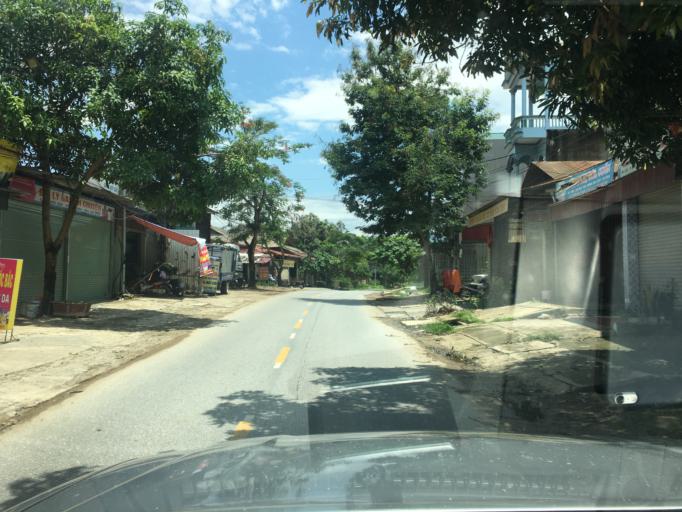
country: VN
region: Yen Bai
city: Son Thinh
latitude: 21.6171
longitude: 104.5082
